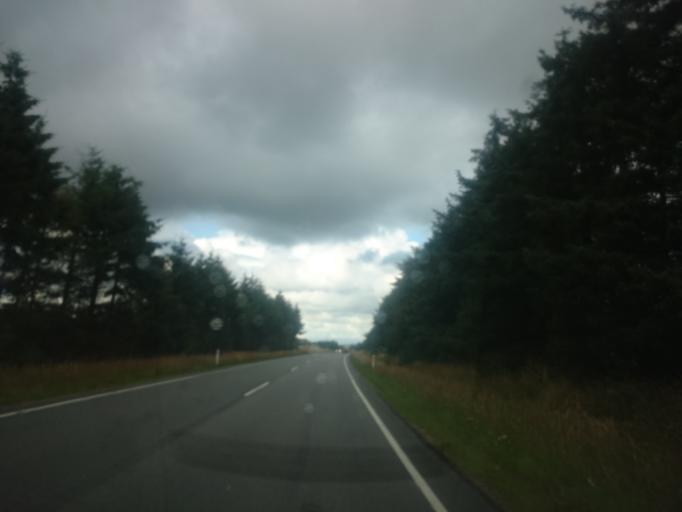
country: DK
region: South Denmark
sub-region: Billund Kommune
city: Grindsted
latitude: 55.6827
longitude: 8.9621
